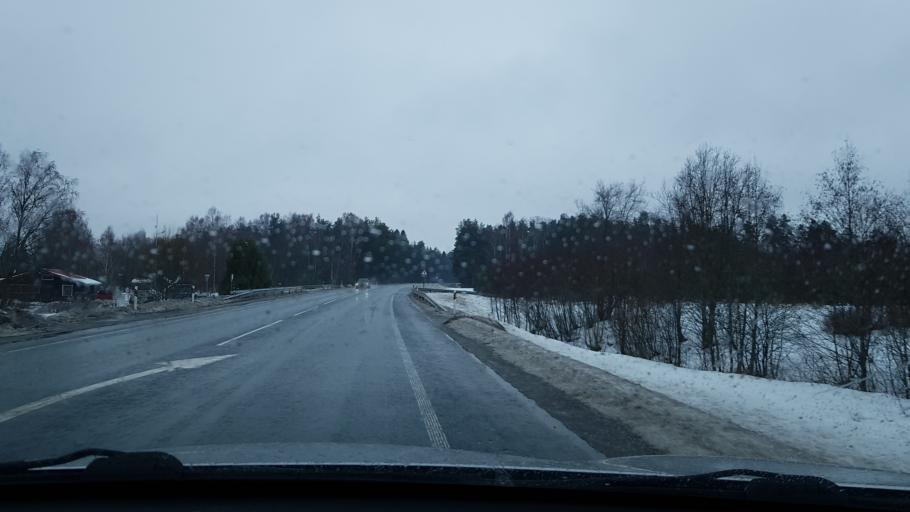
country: EE
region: Raplamaa
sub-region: Kohila vald
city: Kohila
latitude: 59.1612
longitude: 24.7731
